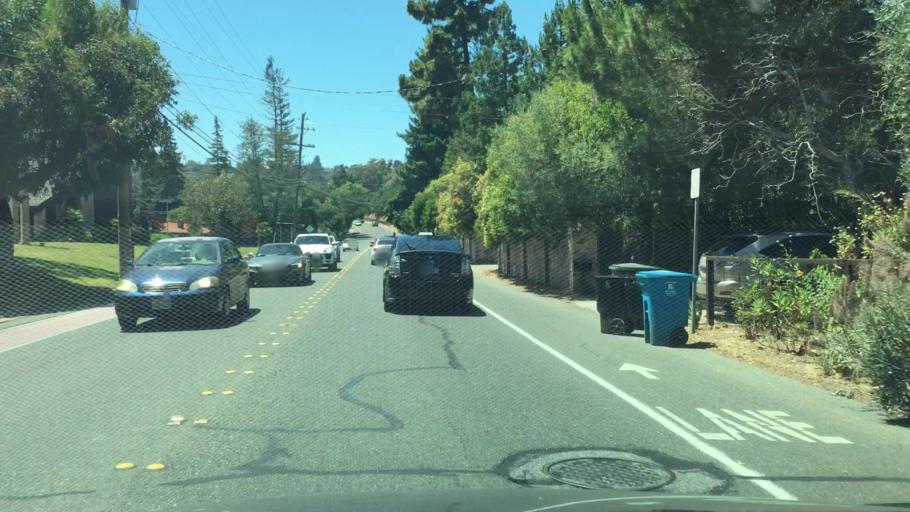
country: US
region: California
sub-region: San Mateo County
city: Emerald Lake Hills
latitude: 37.4796
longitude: -122.2597
